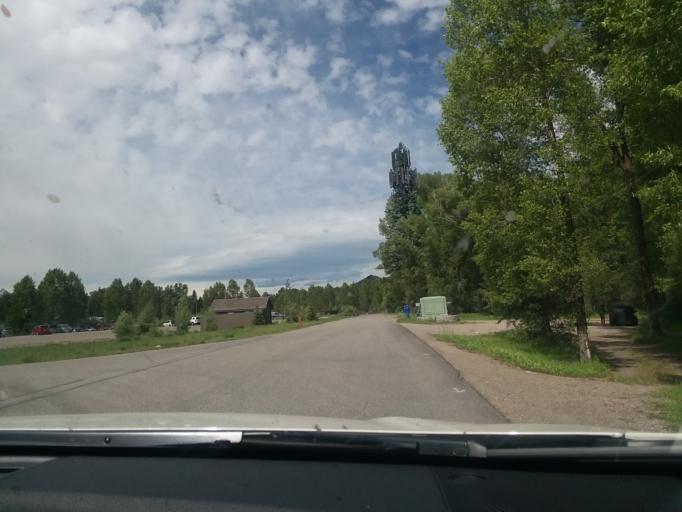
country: US
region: Wyoming
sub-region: Teton County
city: Moose Wilson Road
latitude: 43.4999
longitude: -110.8486
